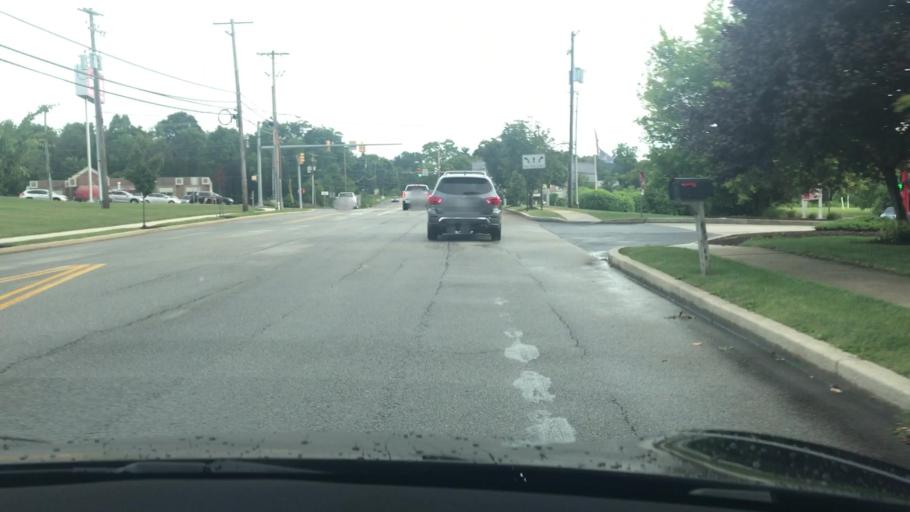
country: US
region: Pennsylvania
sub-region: Dauphin County
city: Lawrence Park
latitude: 40.3369
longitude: -76.8259
